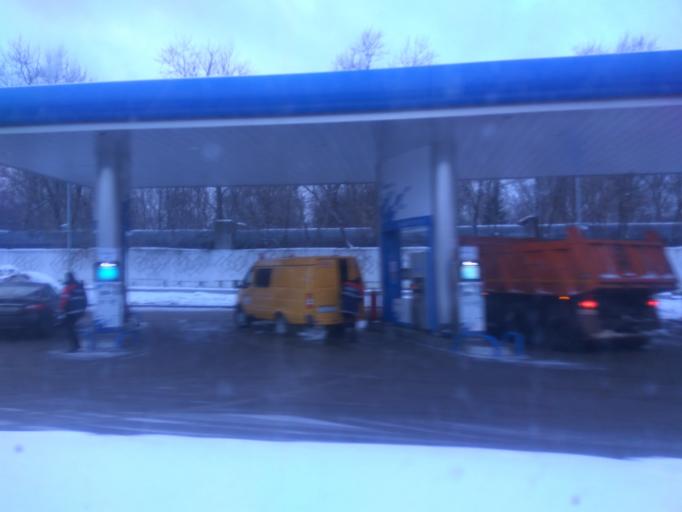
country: RU
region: Moscow
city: Taganskiy
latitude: 55.7324
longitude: 37.6959
